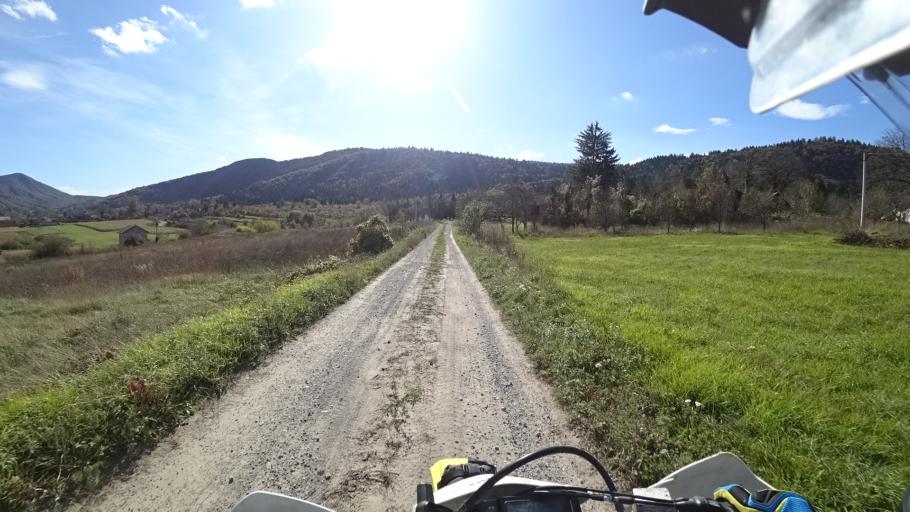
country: HR
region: Karlovacka
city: Plaski
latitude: 45.0733
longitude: 15.3561
